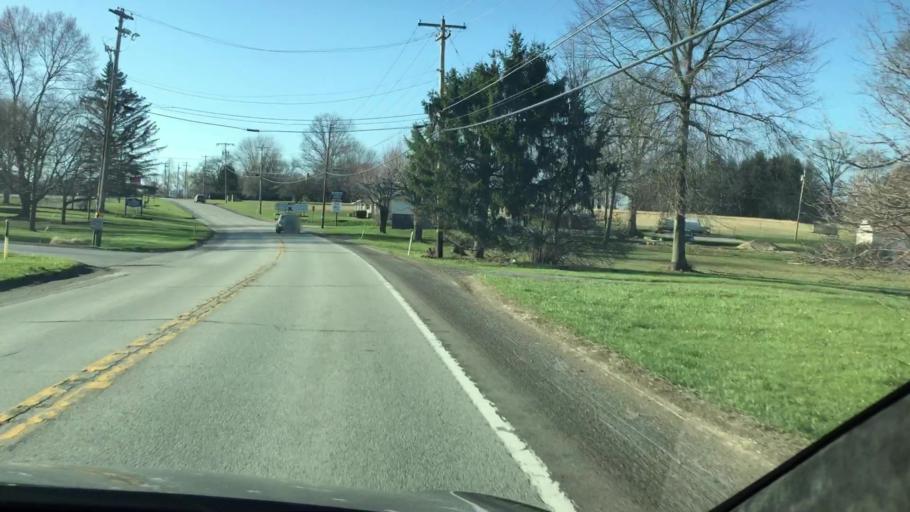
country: US
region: Pennsylvania
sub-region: Butler County
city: Saxonburg
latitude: 40.7417
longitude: -79.7645
